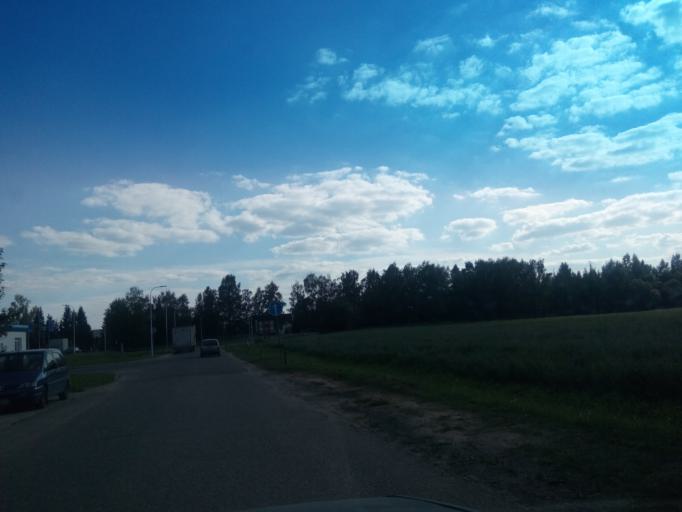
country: BY
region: Vitebsk
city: Navapolatsk
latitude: 55.5440
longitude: 28.6657
